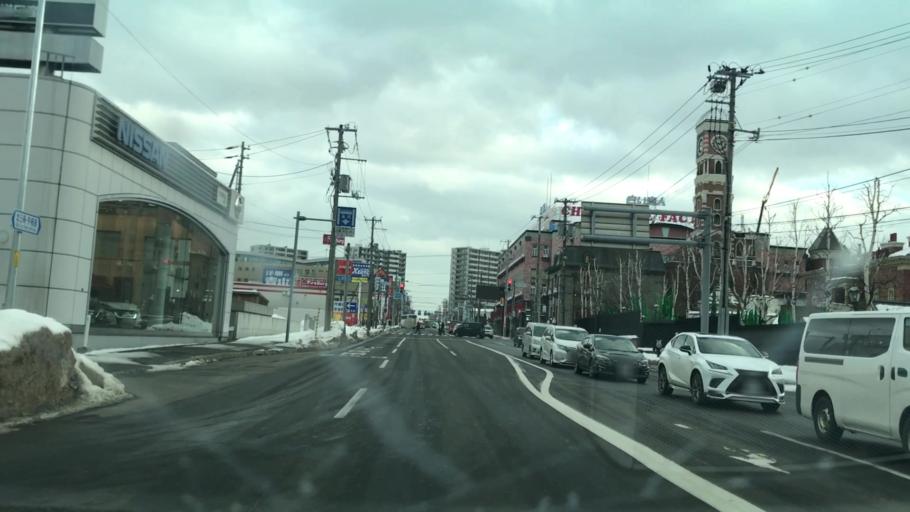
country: JP
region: Hokkaido
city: Sapporo
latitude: 43.0900
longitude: 141.2703
